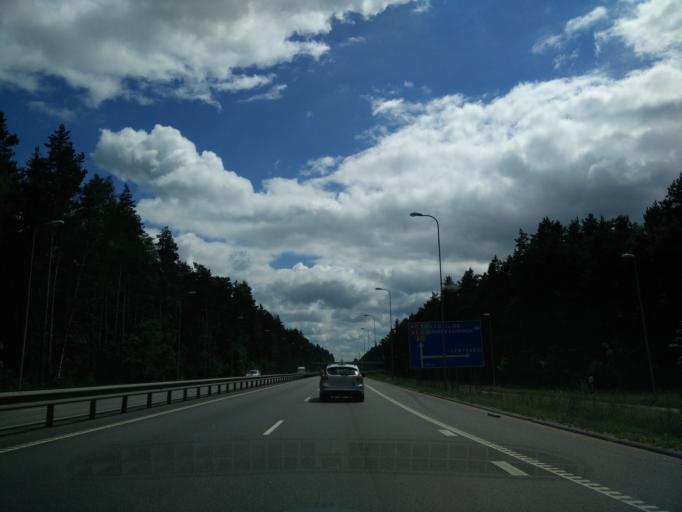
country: LT
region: Vilnius County
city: Lazdynai
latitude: 54.6492
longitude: 25.1507
